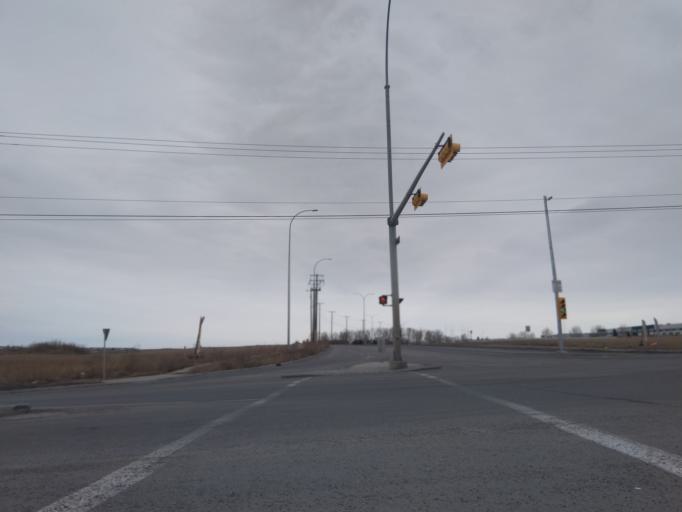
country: CA
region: Alberta
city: Calgary
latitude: 51.1542
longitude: -114.0284
